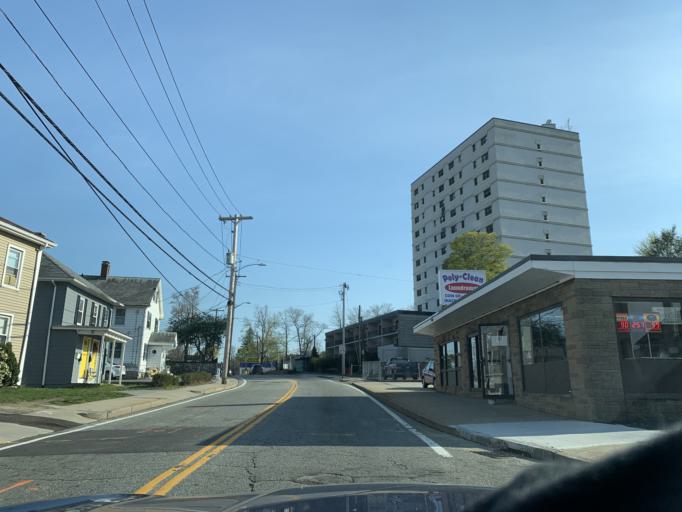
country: US
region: Rhode Island
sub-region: Kent County
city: West Warwick
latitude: 41.7144
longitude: -71.5239
